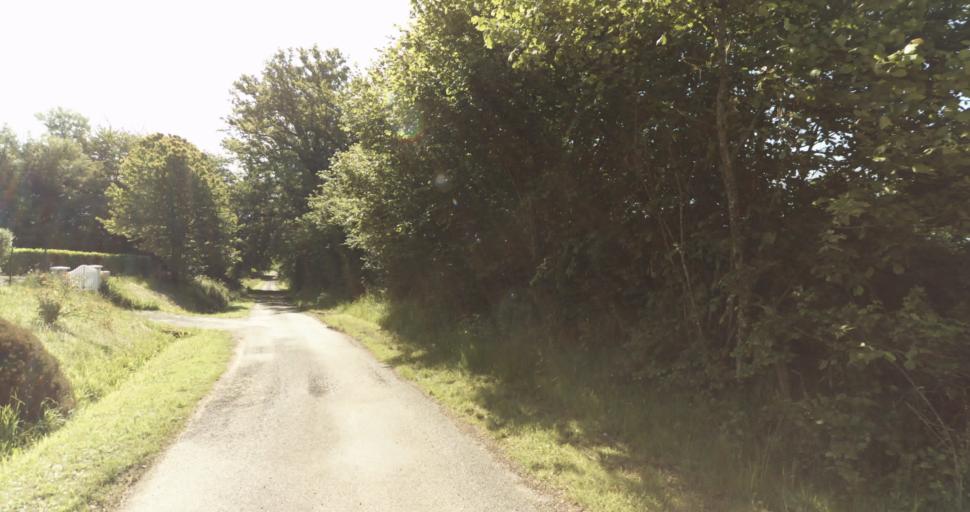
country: FR
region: Limousin
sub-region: Departement de la Haute-Vienne
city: Le Vigen
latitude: 45.7182
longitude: 1.2760
